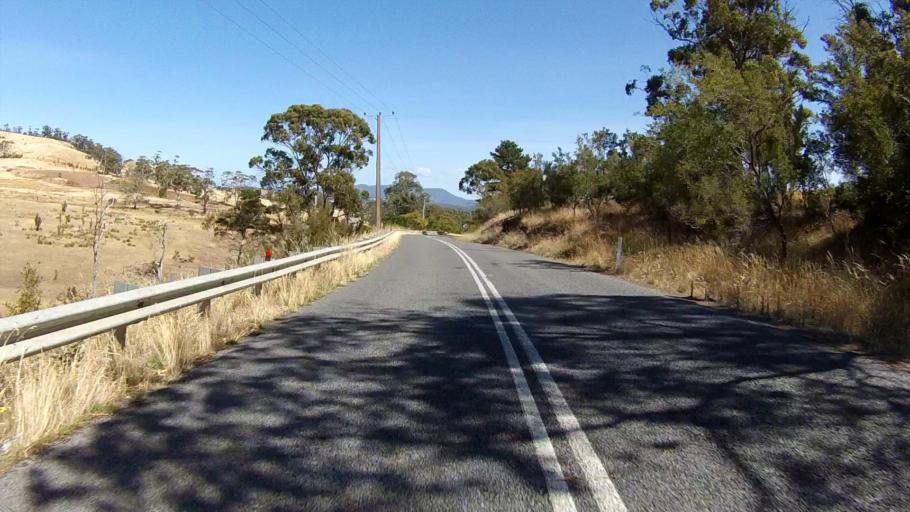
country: AU
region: Tasmania
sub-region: Sorell
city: Sorell
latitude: -42.4929
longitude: 147.9279
